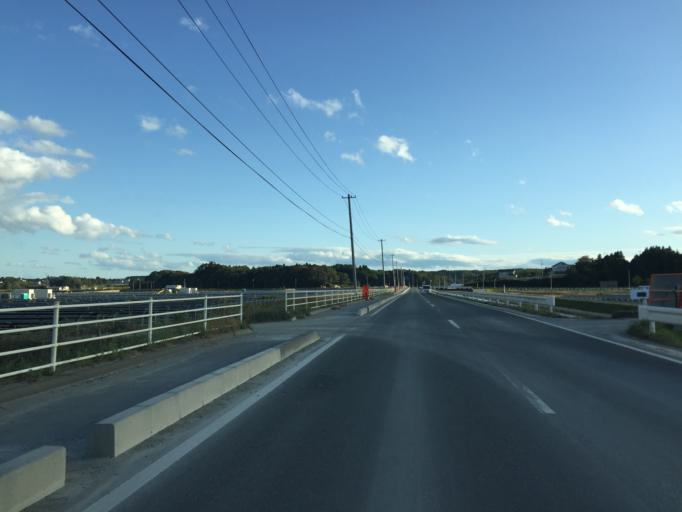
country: JP
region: Miyagi
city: Marumori
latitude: 37.7717
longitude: 140.9815
